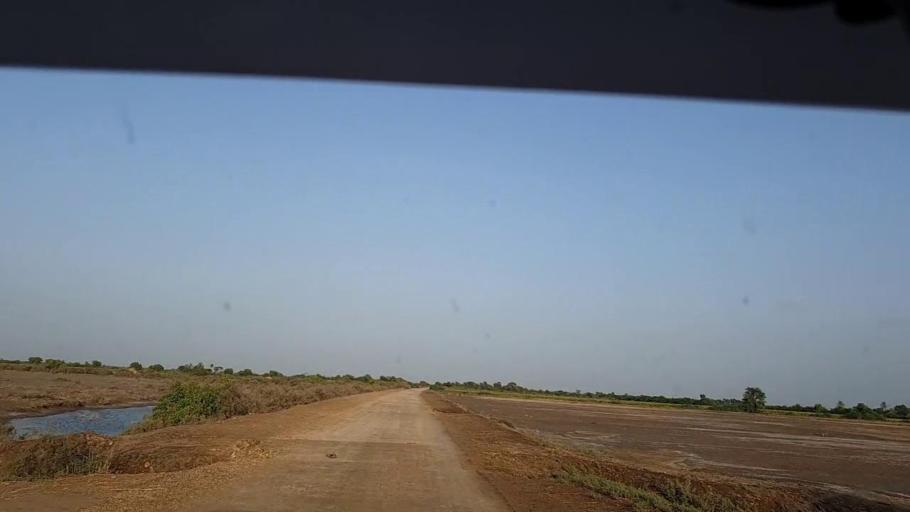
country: PK
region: Sindh
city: Kadhan
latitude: 24.5469
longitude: 68.9318
